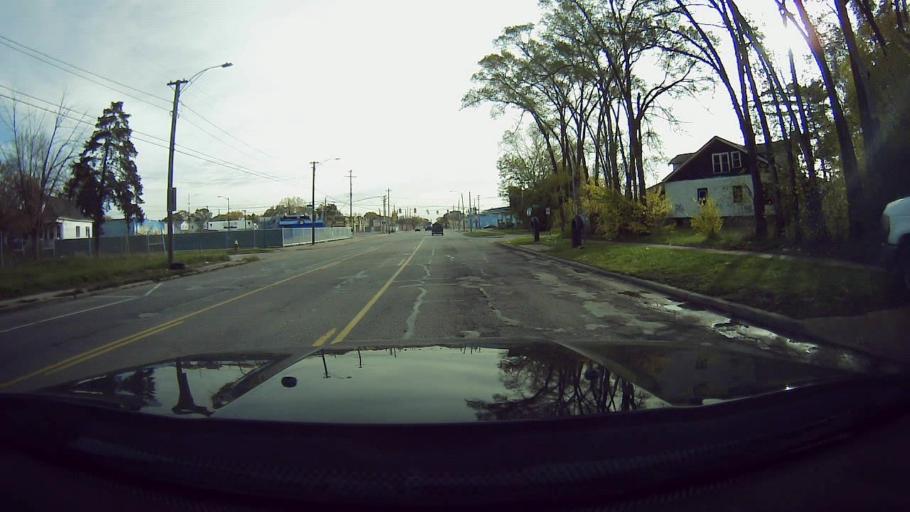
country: US
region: Michigan
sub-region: Wayne County
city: Hamtramck
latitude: 42.4186
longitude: -83.0652
